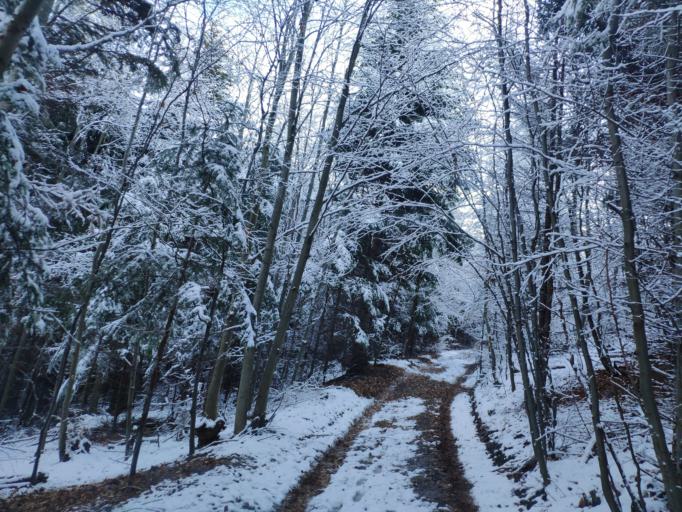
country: SK
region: Kosicky
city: Moldava nad Bodvou
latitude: 48.7462
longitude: 21.0893
